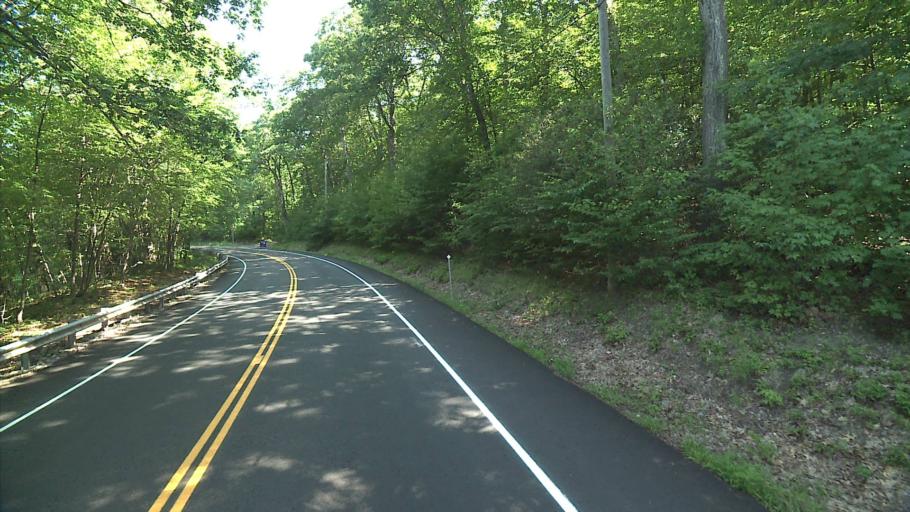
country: US
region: Connecticut
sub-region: Litchfield County
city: Terryville
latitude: 41.7436
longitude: -73.0169
